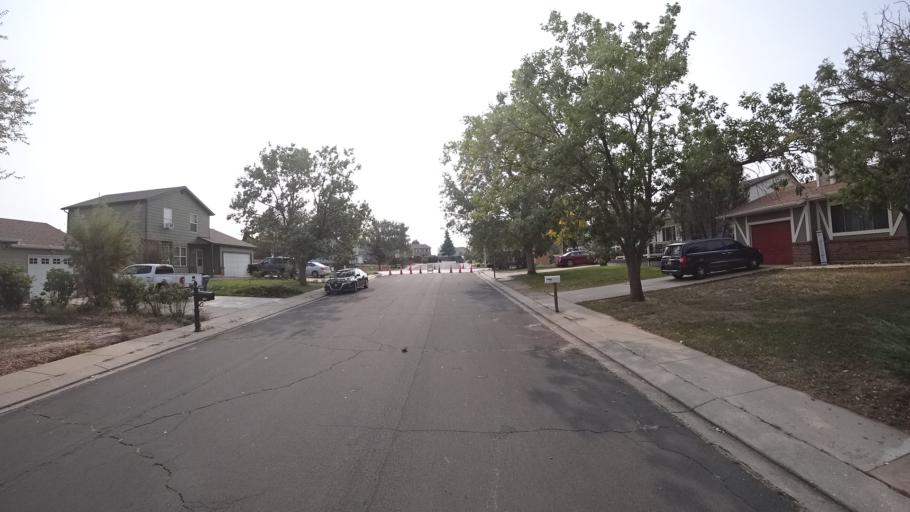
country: US
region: Colorado
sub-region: El Paso County
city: Stratmoor
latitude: 38.8068
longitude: -104.7440
